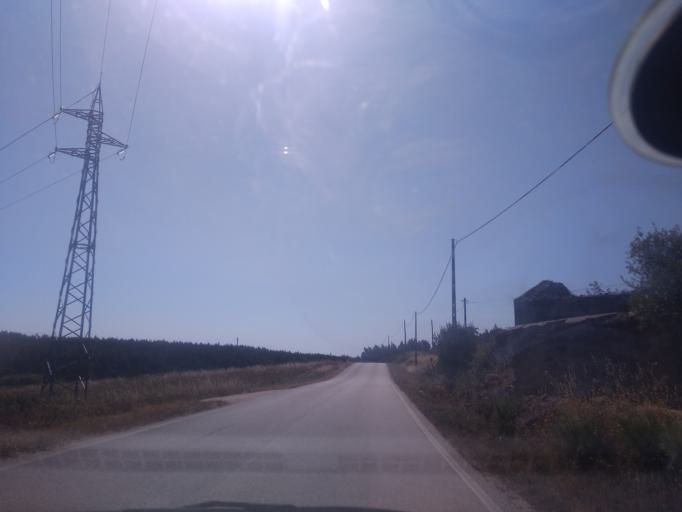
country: PT
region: Faro
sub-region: Aljezur
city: Aljezur
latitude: 37.2197
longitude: -8.7959
